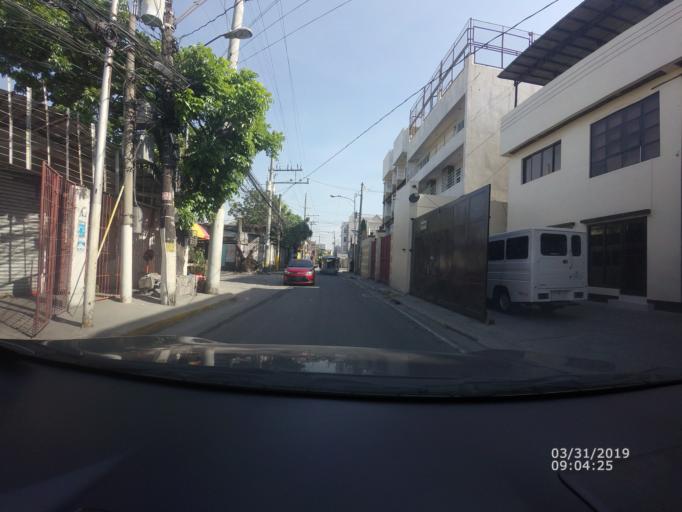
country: PH
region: Metro Manila
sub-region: Mandaluyong
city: Mandaluyong City
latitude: 14.5810
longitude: 121.0209
